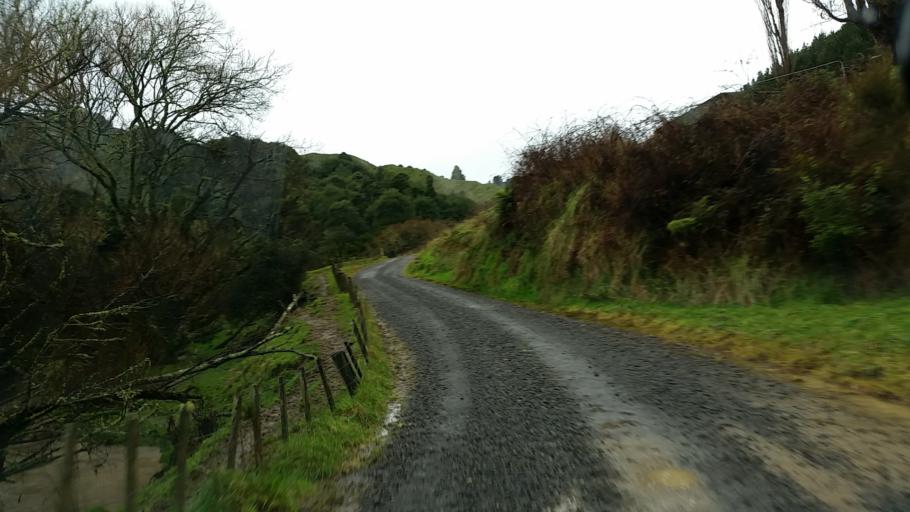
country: NZ
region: Taranaki
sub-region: South Taranaki District
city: Eltham
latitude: -39.5019
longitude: 174.4232
